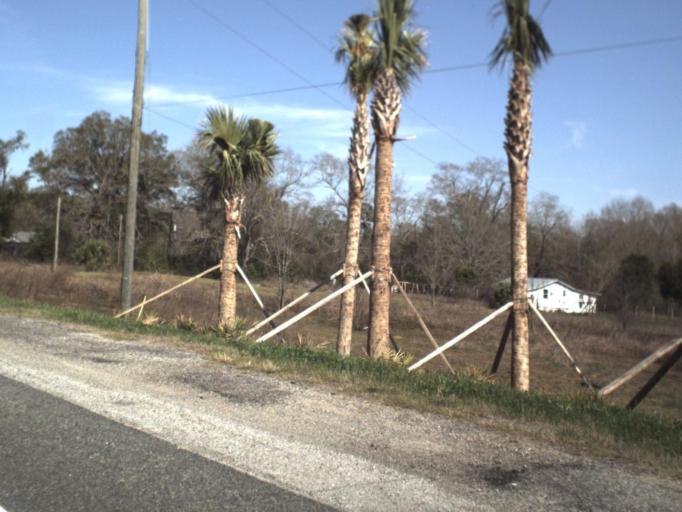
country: US
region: Alabama
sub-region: Houston County
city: Cottonwood
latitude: 30.9973
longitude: -85.4075
